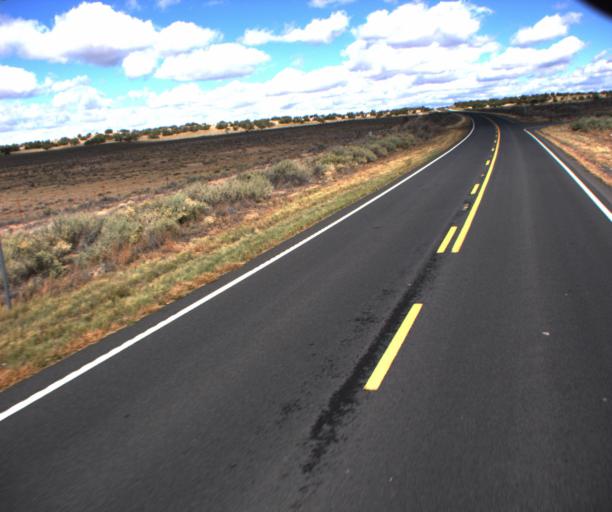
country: US
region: Arizona
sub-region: Apache County
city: Houck
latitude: 35.0964
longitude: -109.3124
